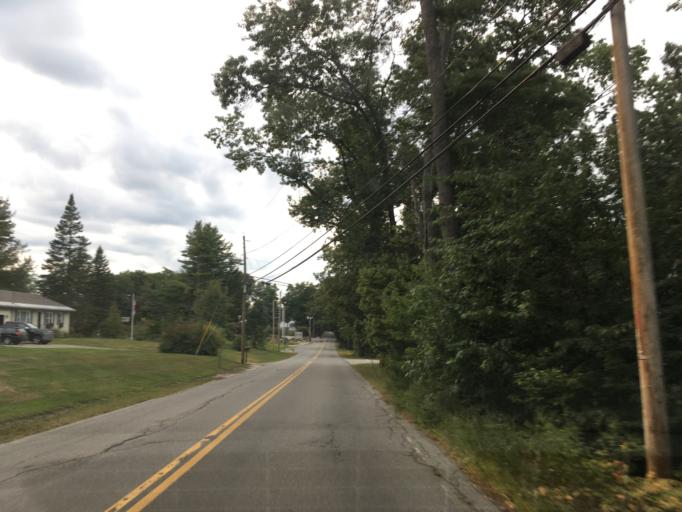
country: US
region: New Hampshire
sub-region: Rockingham County
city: Exeter
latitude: 43.0107
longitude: -70.9131
